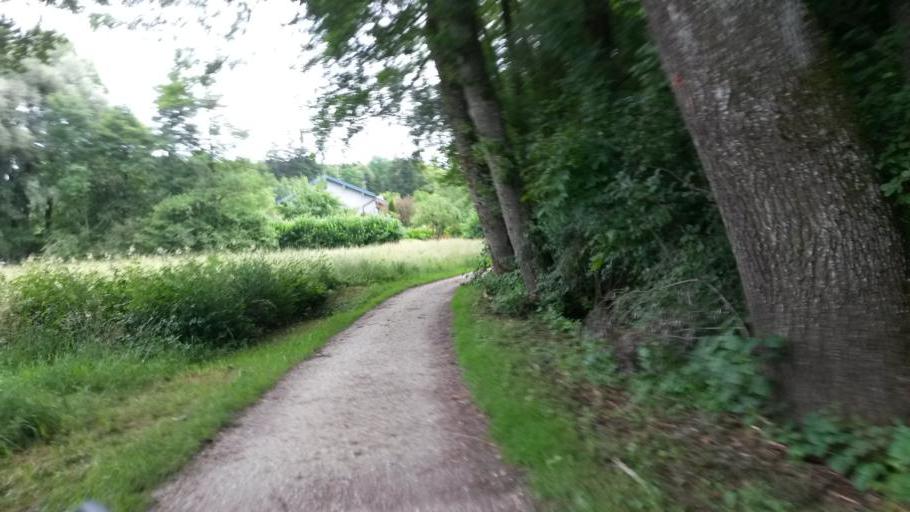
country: DE
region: Bavaria
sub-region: Upper Bavaria
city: Gstadt am Chiemsee
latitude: 47.8880
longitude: 12.3793
